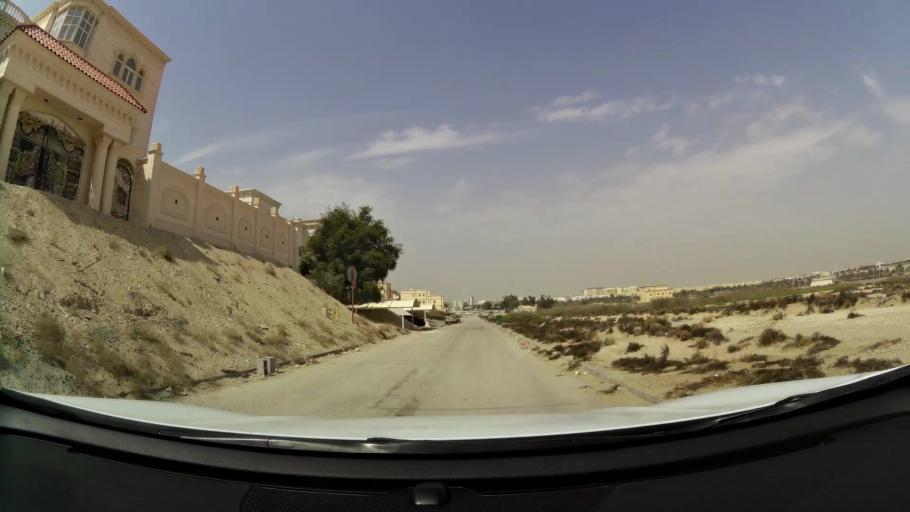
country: AE
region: Abu Dhabi
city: Abu Dhabi
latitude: 24.3009
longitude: 54.6306
